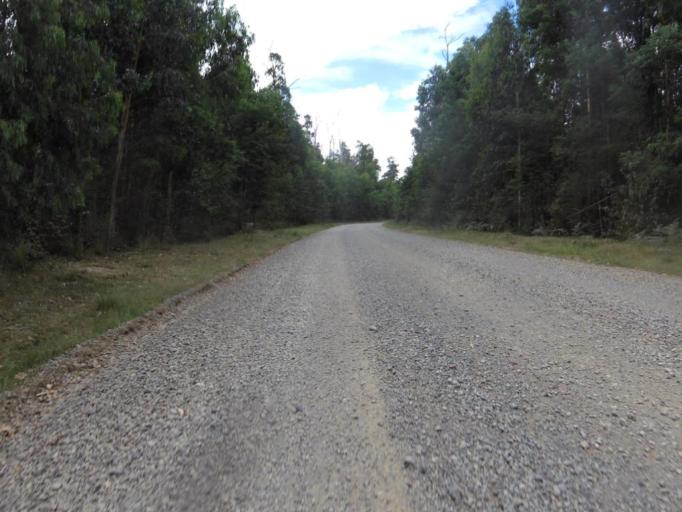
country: AU
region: Victoria
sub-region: Murrindindi
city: Alexandra
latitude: -37.3995
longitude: 145.5592
